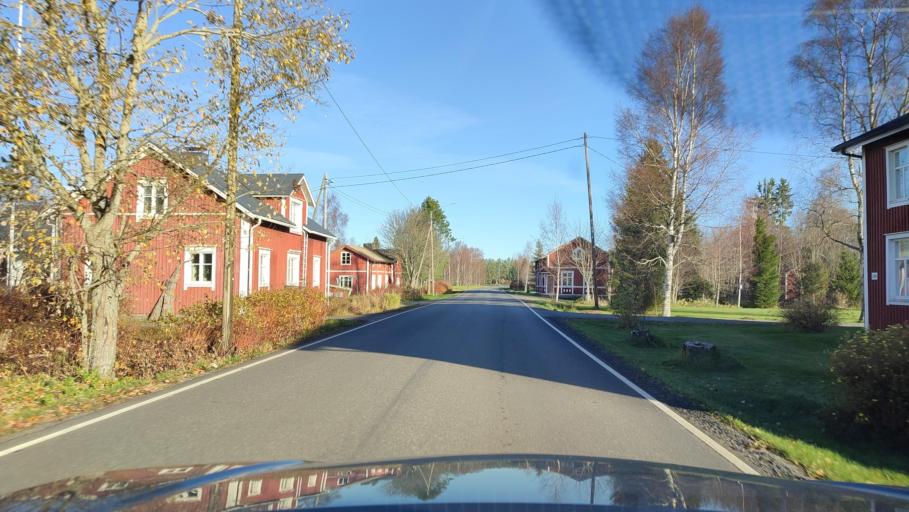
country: FI
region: Southern Ostrobothnia
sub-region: Suupohja
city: Karijoki
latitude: 62.2776
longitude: 21.7082
